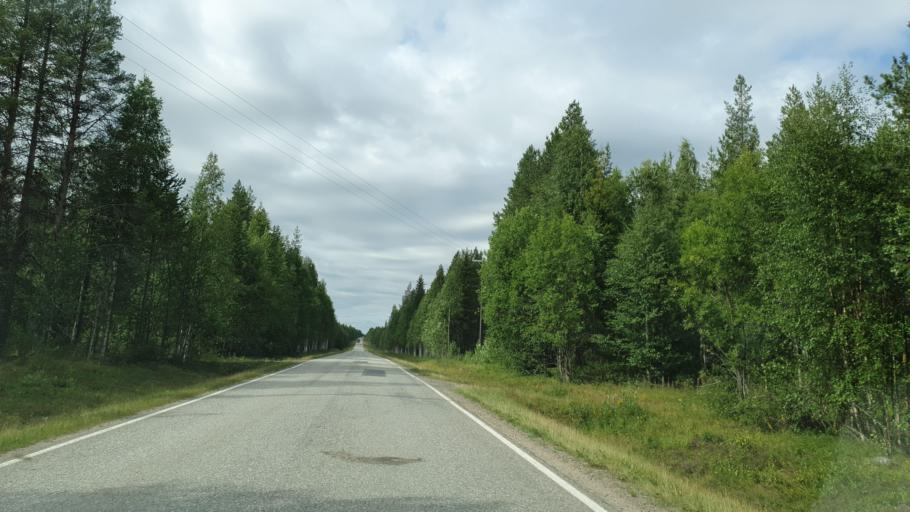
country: FI
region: Lapland
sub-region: Tunturi-Lappi
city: Kittilae
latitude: 67.6155
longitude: 25.3303
